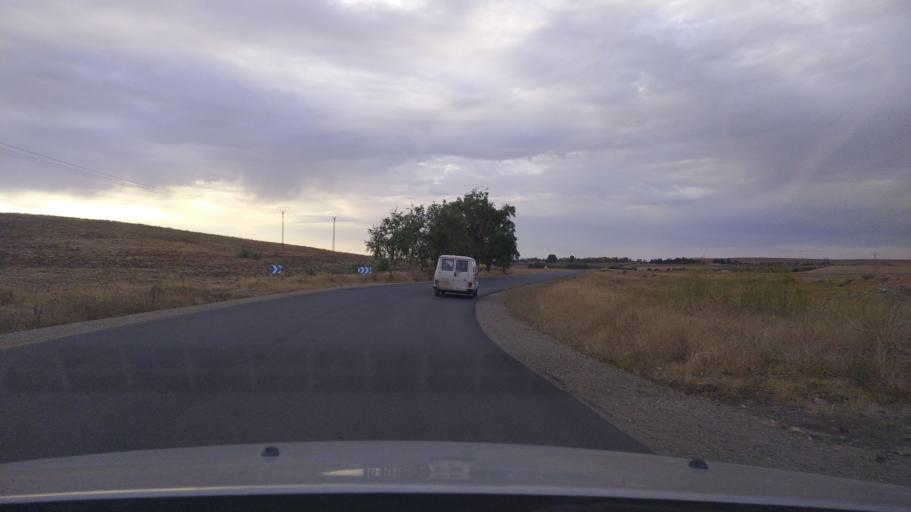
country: DZ
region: Tiaret
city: Frenda
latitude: 35.0141
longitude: 1.1132
